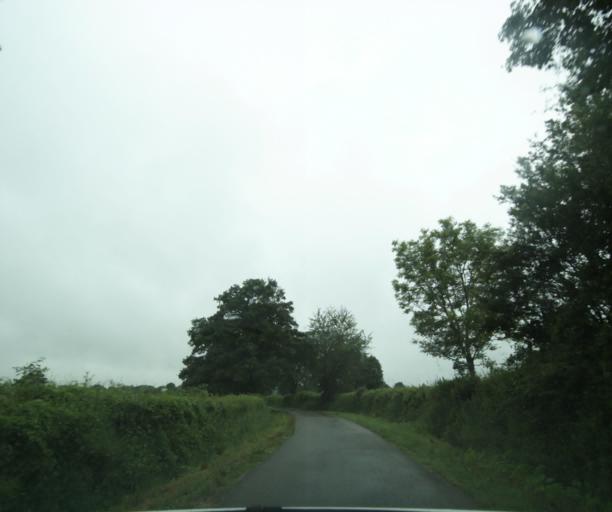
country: FR
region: Bourgogne
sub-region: Departement de Saone-et-Loire
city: Charolles
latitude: 46.4648
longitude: 4.2055
